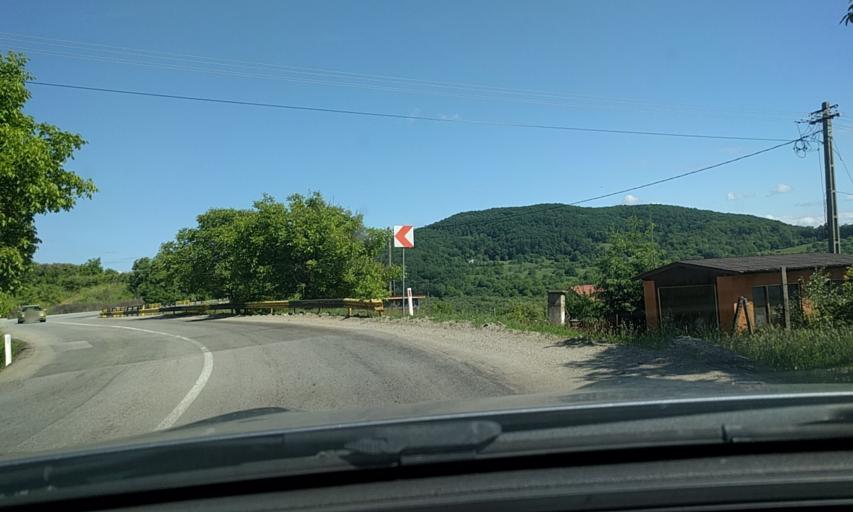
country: RO
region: Bistrita-Nasaud
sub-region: Comuna Dumitra
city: Dumitra
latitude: 47.1784
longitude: 24.4909
